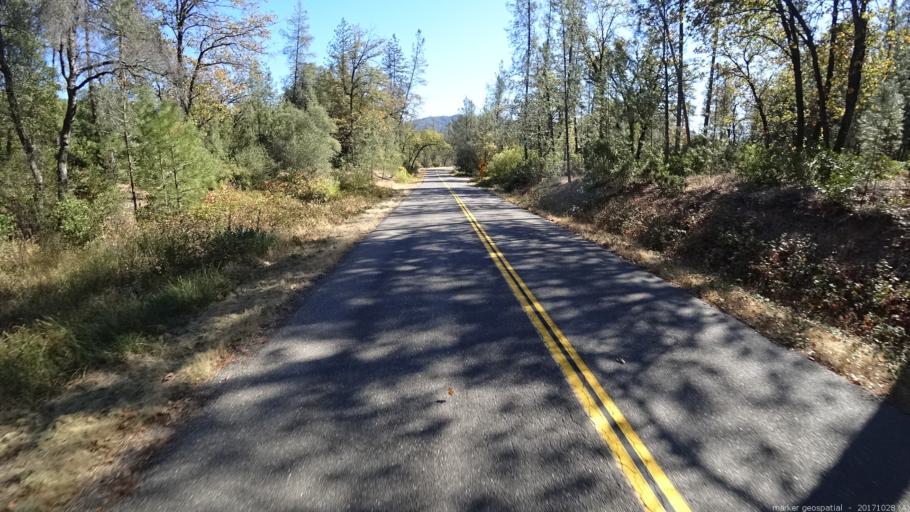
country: US
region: California
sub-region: Shasta County
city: Shasta
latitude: 40.5846
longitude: -122.5366
